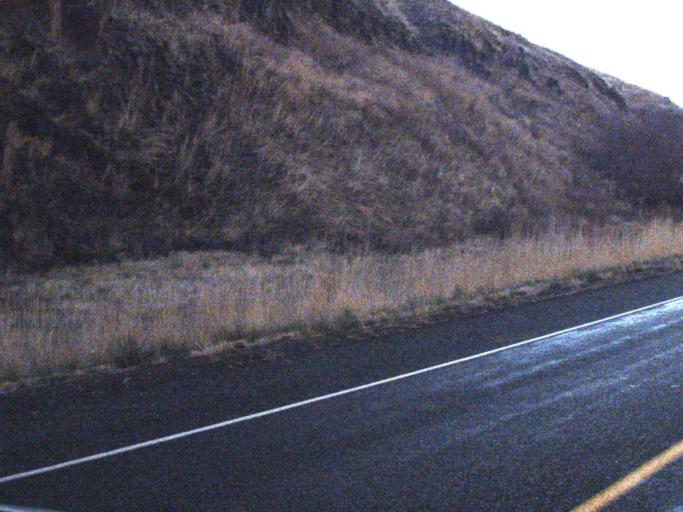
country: US
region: Washington
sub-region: Garfield County
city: Pomeroy
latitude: 46.6024
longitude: -117.7844
